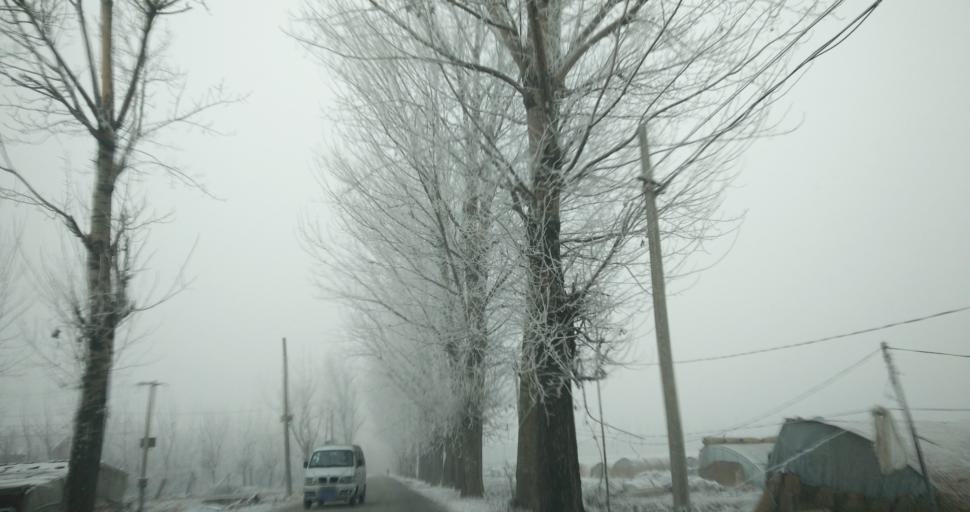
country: CN
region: Beijing
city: Yinghai
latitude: 39.7065
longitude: 116.4289
